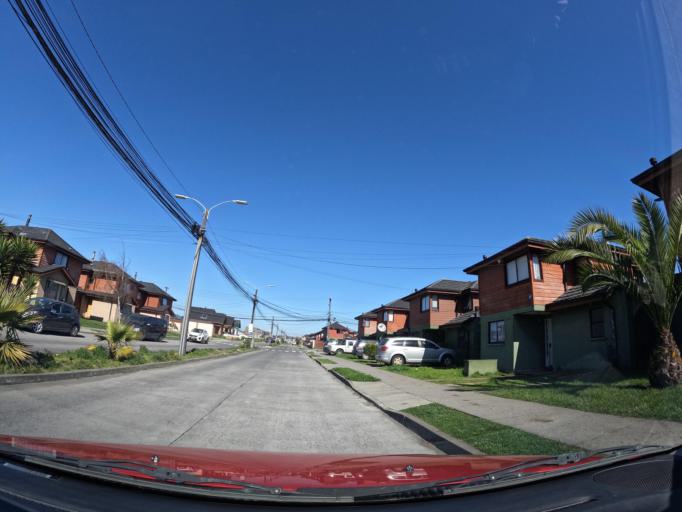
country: CL
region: Biobio
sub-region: Provincia de Concepcion
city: Concepcion
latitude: -36.8874
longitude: -73.1456
